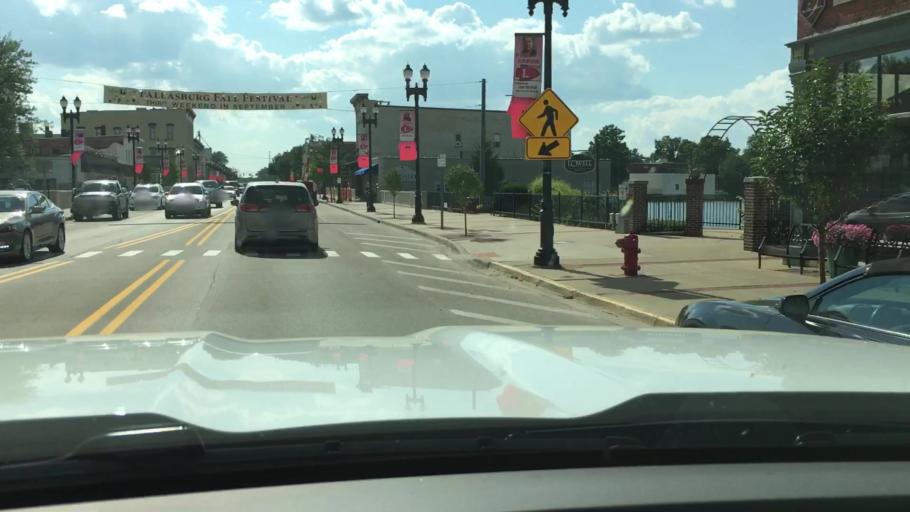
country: US
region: Michigan
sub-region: Kent County
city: Lowell
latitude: 42.9345
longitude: -85.3376
